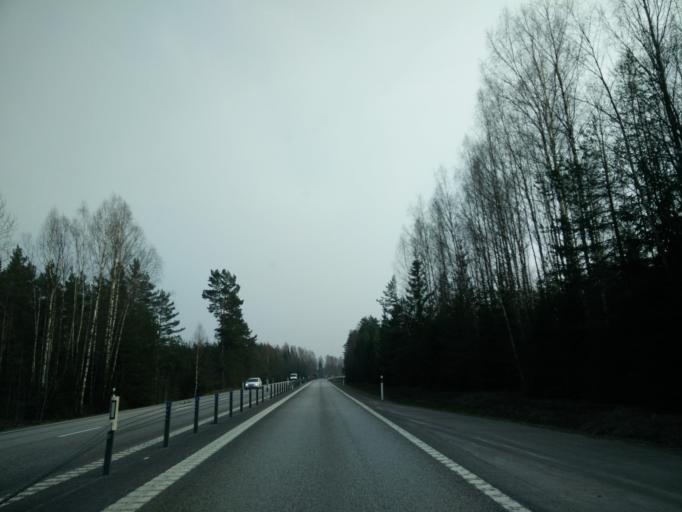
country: SE
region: Vaermland
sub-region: Forshaga Kommun
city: Forshaga
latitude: 59.4677
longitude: 13.4138
